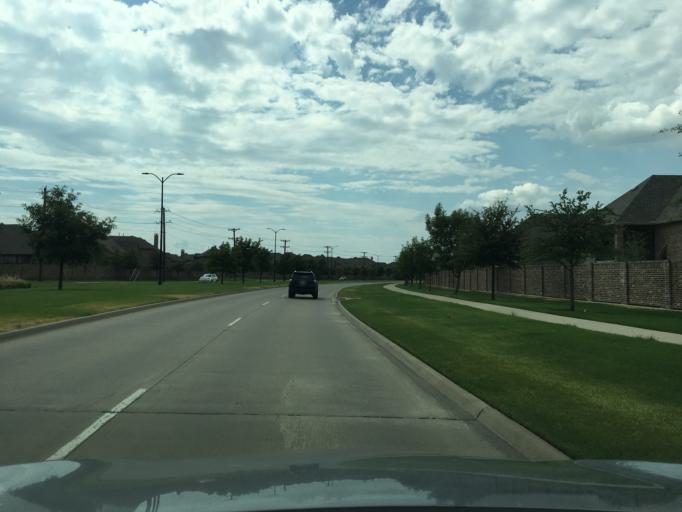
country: US
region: Texas
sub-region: Denton County
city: The Colony
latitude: 33.1332
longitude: -96.8736
